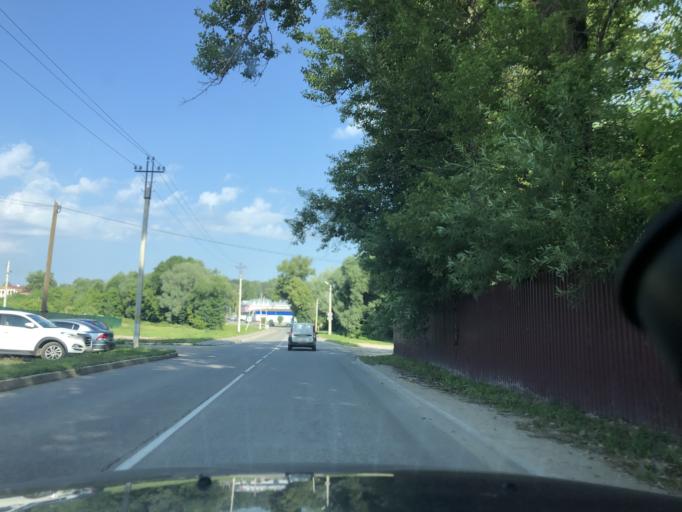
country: RU
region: Tula
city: Dubna
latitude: 54.1497
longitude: 36.9691
